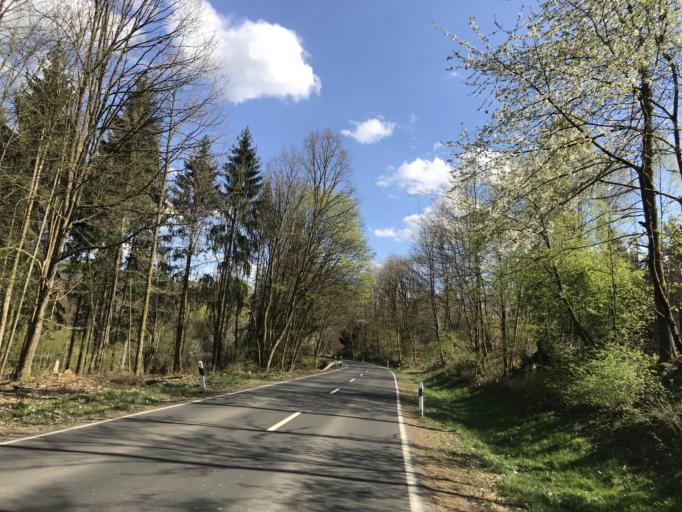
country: DE
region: Hesse
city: Beuern
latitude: 50.6504
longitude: 8.8235
